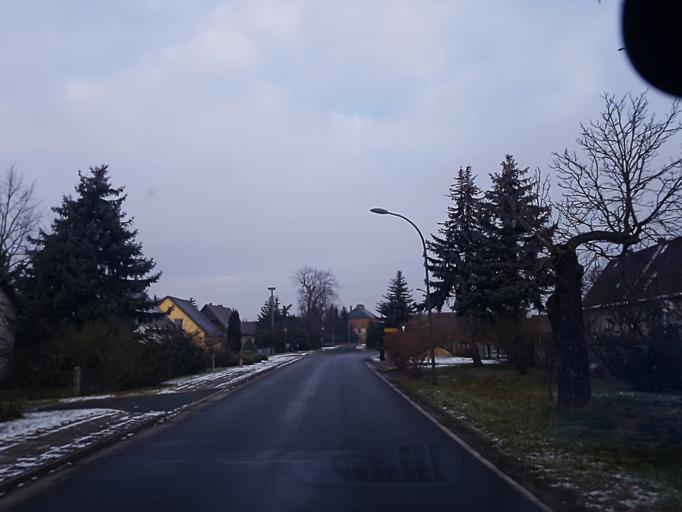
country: DE
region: Brandenburg
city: Crinitz
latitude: 51.7604
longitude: 13.8576
